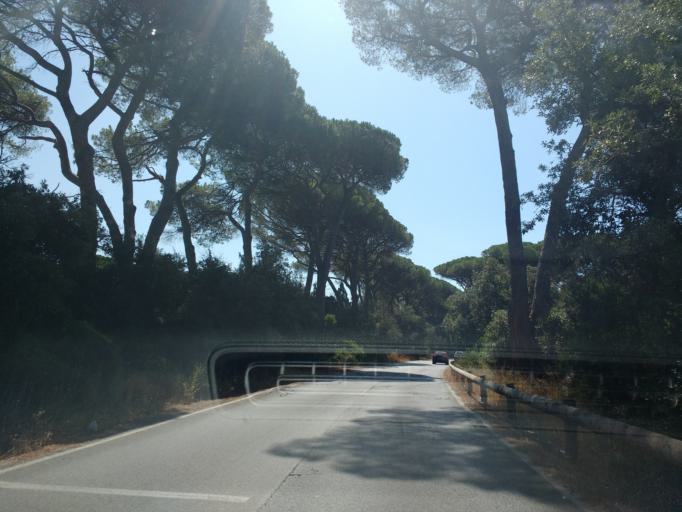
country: IT
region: Latium
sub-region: Citta metropolitana di Roma Capitale
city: Acilia-Castel Fusano-Ostia Antica
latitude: 41.7249
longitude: 12.3427
